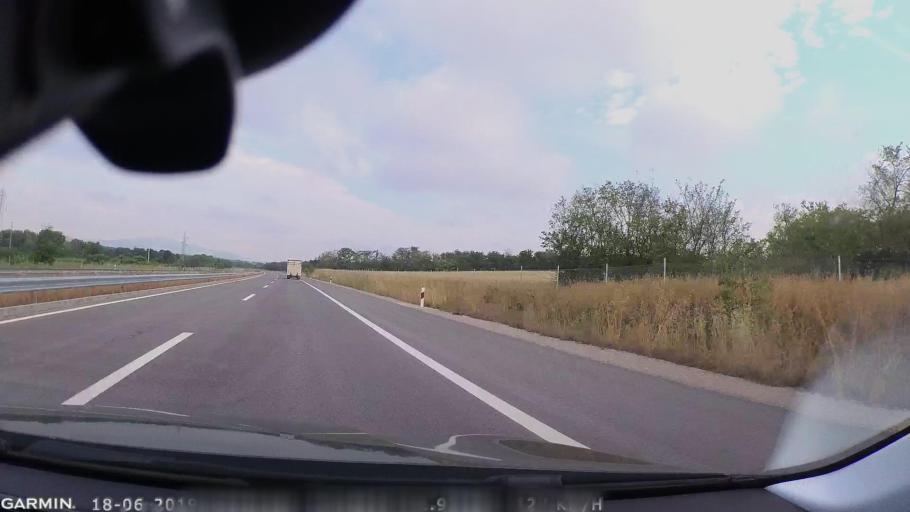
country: MK
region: Sveti Nikole
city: Sveti Nikole
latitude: 41.8437
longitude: 21.9776
